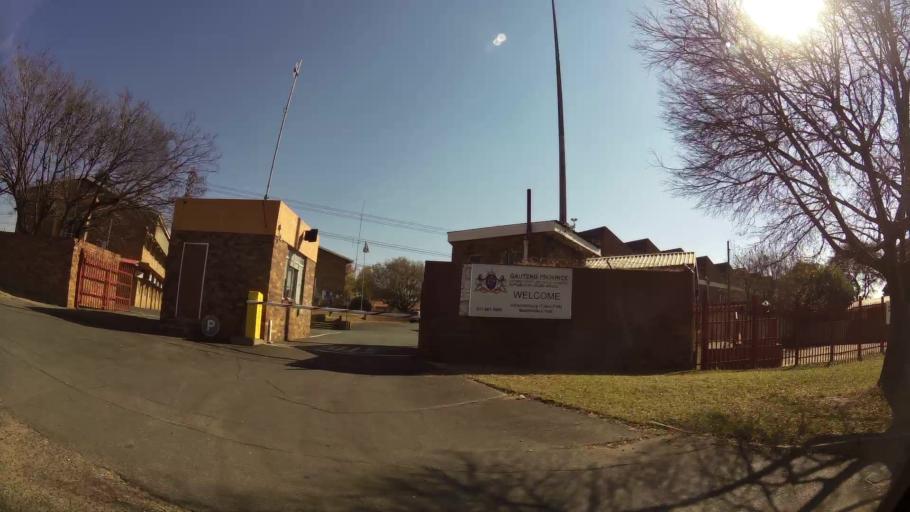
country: ZA
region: Gauteng
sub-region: City of Johannesburg Metropolitan Municipality
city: Johannesburg
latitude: -26.2502
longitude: 28.0999
